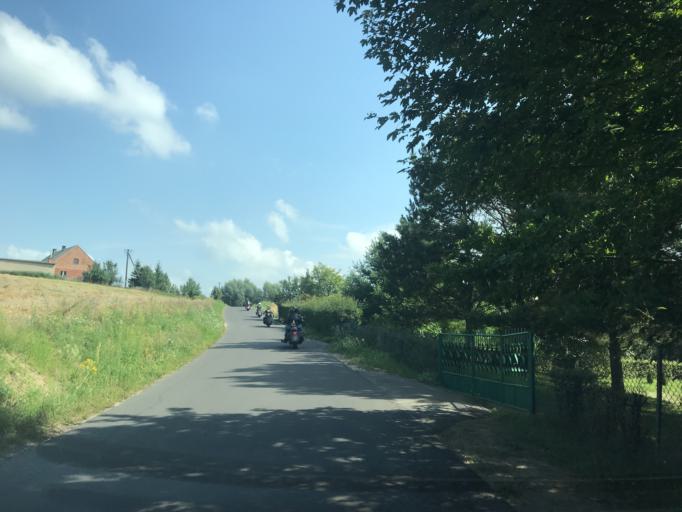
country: PL
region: Warmian-Masurian Voivodeship
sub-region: Powiat nowomiejski
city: Biskupiec
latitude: 53.4524
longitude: 19.4520
